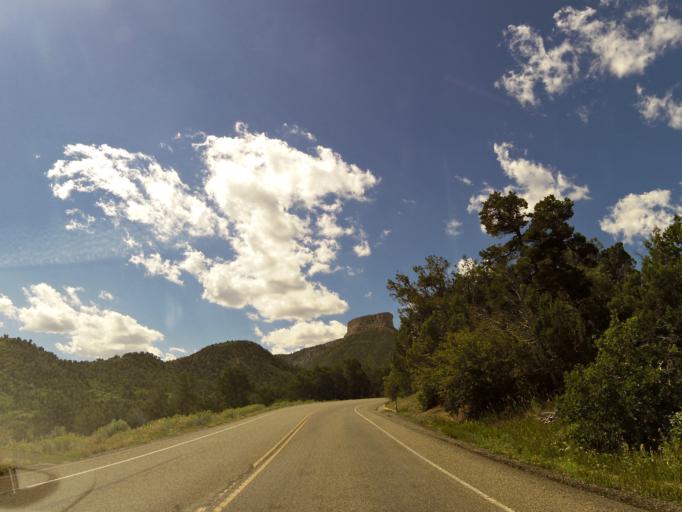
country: US
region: Colorado
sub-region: Montezuma County
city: Mancos
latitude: 37.3345
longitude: -108.4121
